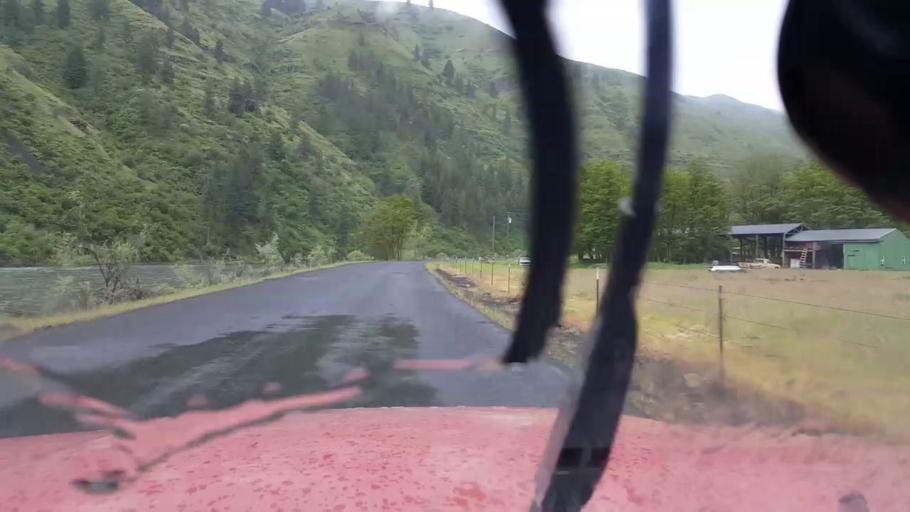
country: US
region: Washington
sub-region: Asotin County
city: Asotin
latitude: 46.0377
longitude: -117.2671
